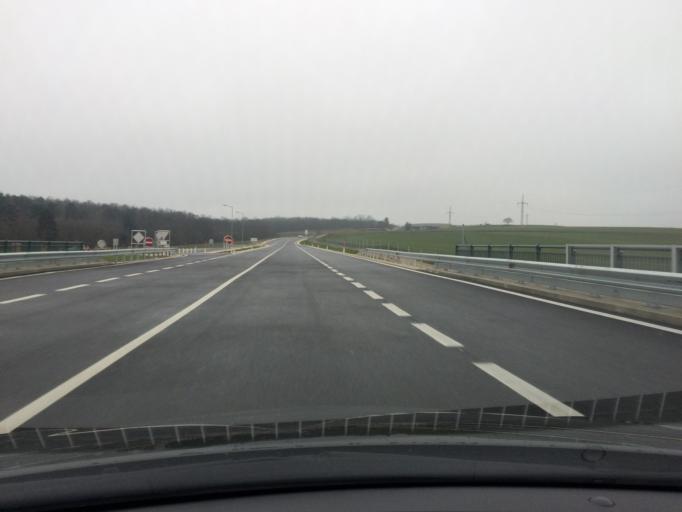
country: AT
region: Lower Austria
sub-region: Politischer Bezirk Mistelbach
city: Mistelbach
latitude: 48.5499
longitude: 16.5873
